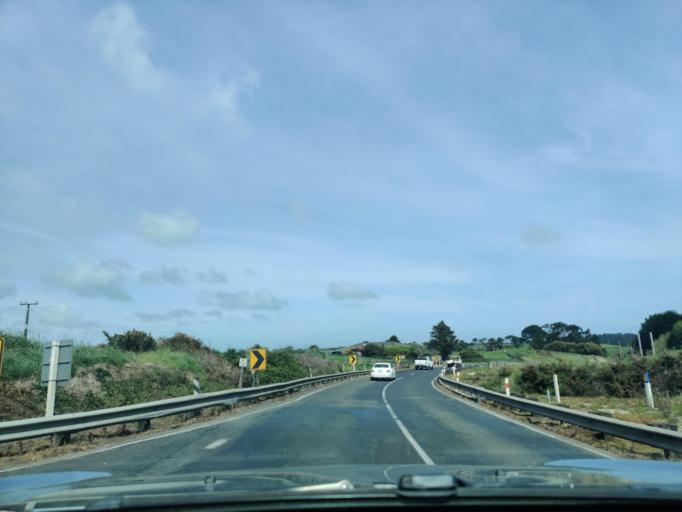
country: NZ
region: Taranaki
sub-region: South Taranaki District
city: Hawera
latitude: -39.6313
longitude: 174.3771
